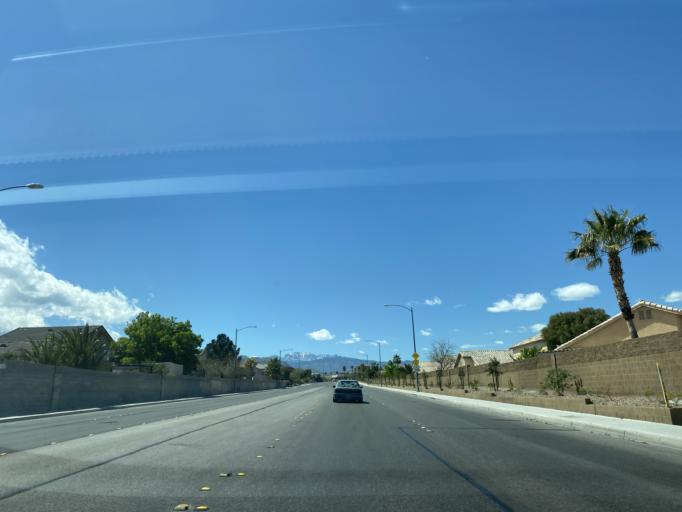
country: US
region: Nevada
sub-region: Clark County
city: Las Vegas
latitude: 36.2989
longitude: -115.2744
